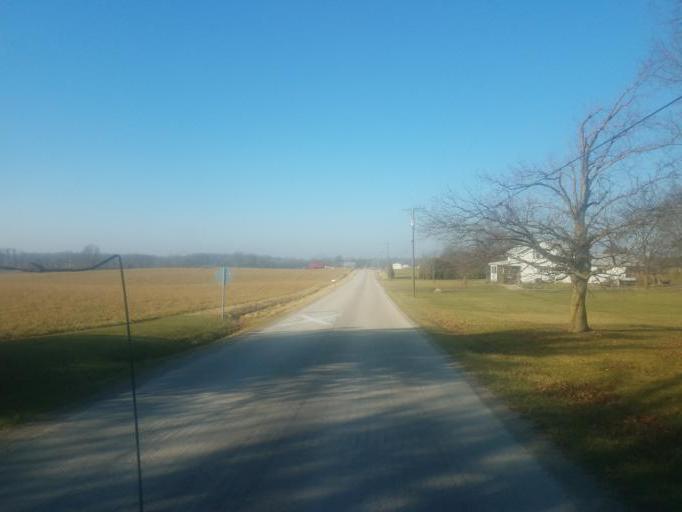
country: US
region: Ohio
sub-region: Crawford County
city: Bucyrus
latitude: 40.8997
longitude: -82.9471
